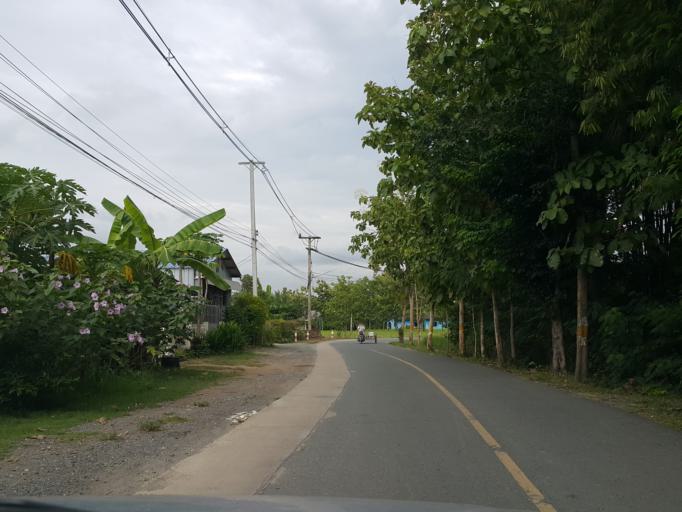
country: TH
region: Chiang Mai
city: San Sai
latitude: 18.8424
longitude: 99.1453
